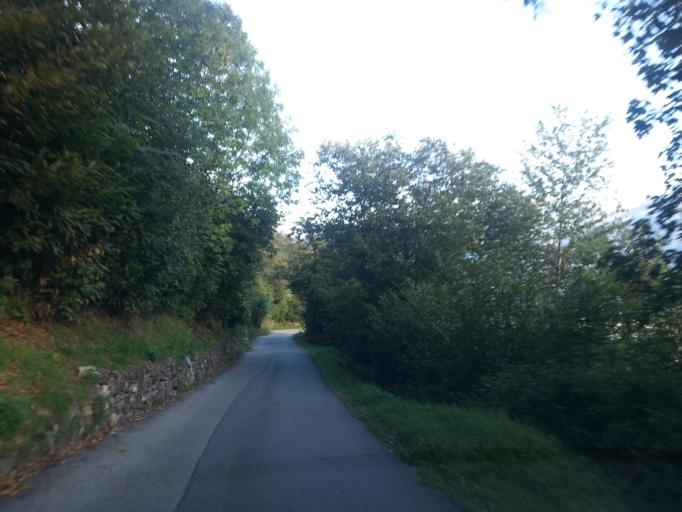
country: IT
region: Lombardy
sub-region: Provincia di Como
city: Sorico
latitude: 46.1839
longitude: 9.3857
